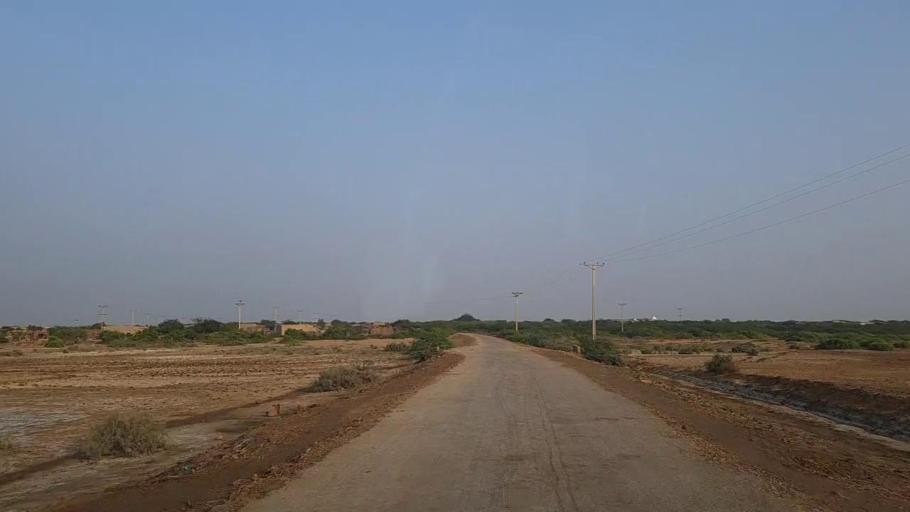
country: PK
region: Sindh
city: Thatta
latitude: 24.6902
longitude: 67.8142
